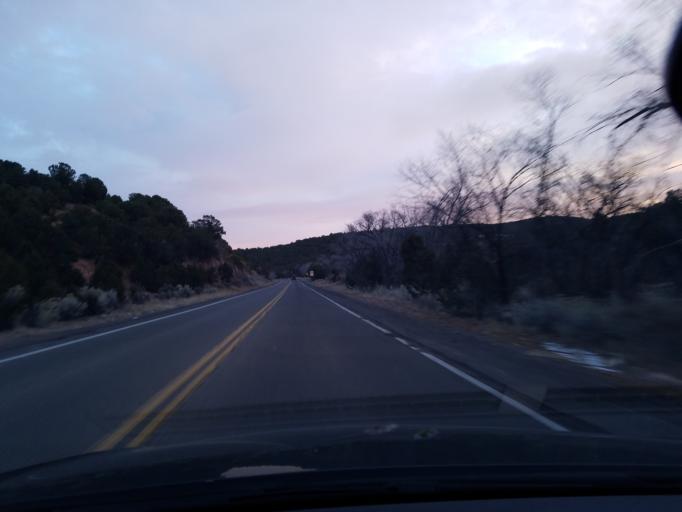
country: US
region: New Mexico
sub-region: Santa Fe County
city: Santa Fe
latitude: 35.7055
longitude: -105.9033
